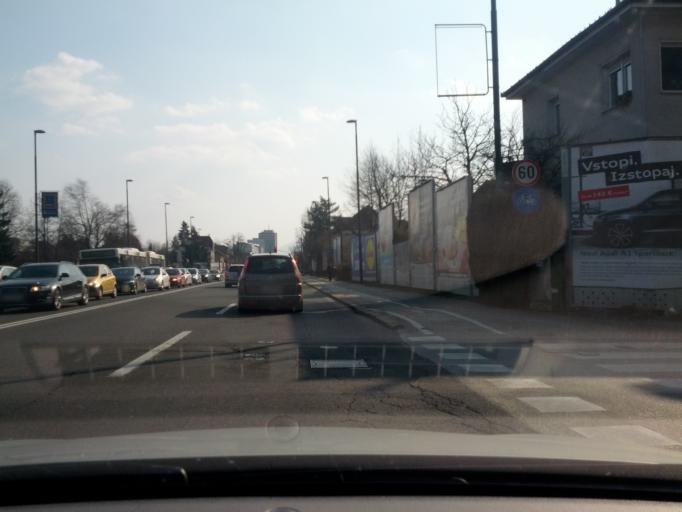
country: SI
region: Ljubljana
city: Ljubljana
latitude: 46.0731
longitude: 14.5110
